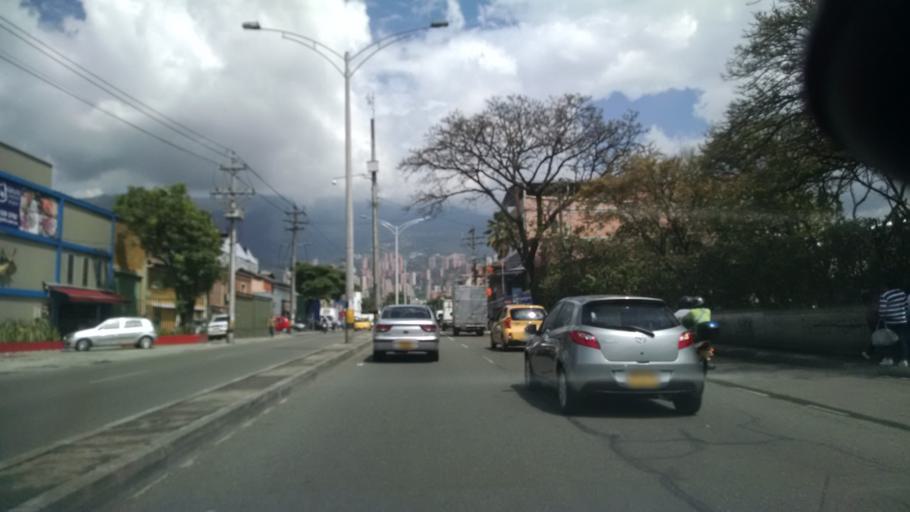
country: CO
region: Antioquia
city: Itagui
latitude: 6.2163
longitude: -75.5845
